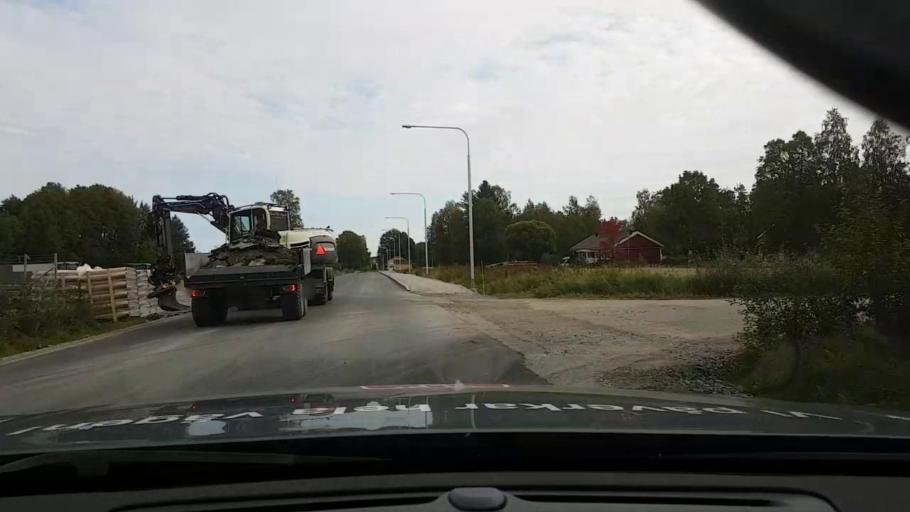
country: SE
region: Vaesternorrland
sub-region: OErnskoeldsviks Kommun
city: Bjasta
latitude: 63.2891
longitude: 18.4417
